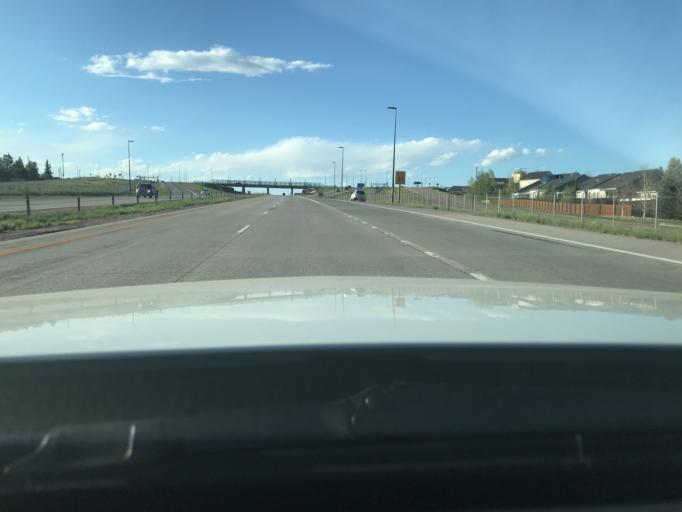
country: US
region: Wyoming
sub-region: Laramie County
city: Cheyenne
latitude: 41.1796
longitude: -104.8379
